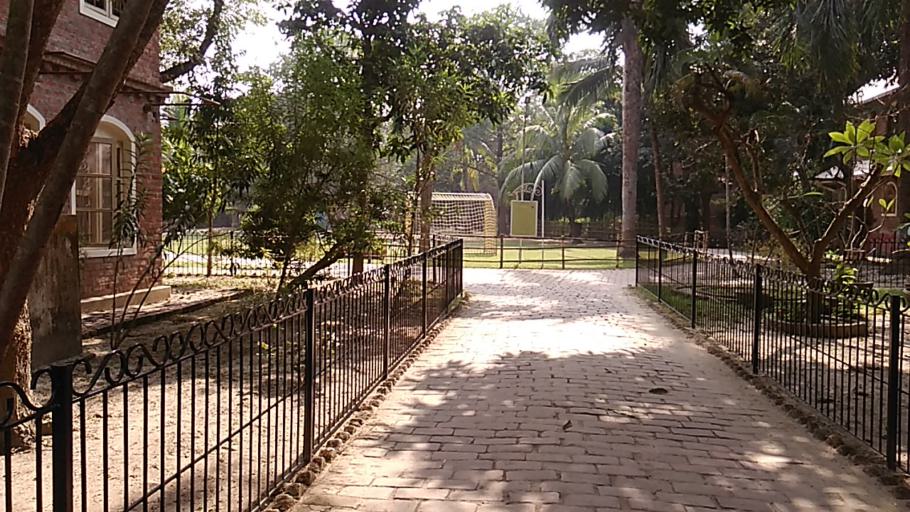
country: IN
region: West Bengal
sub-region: Nadia
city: Navadwip
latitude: 23.4222
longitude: 88.3879
